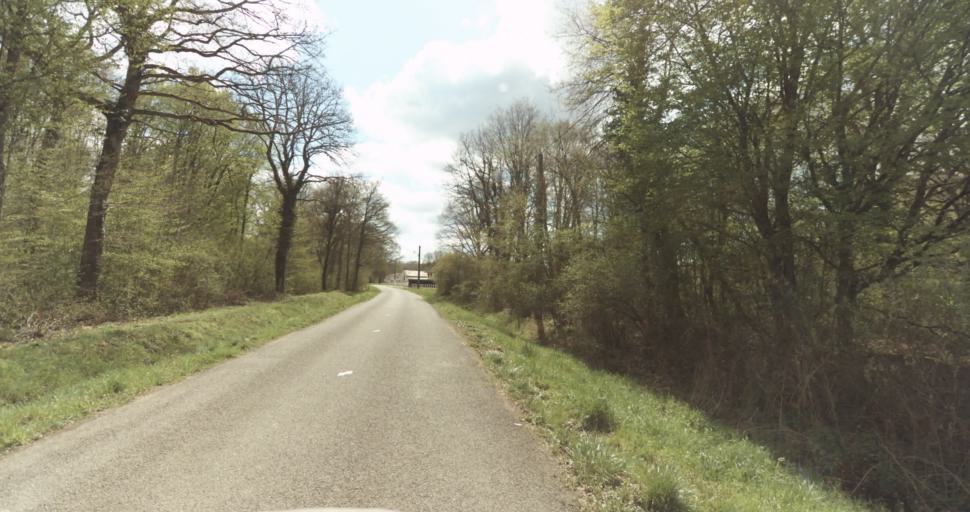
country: FR
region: Bourgogne
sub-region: Departement de la Cote-d'Or
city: Auxonne
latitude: 47.1774
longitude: 5.4221
